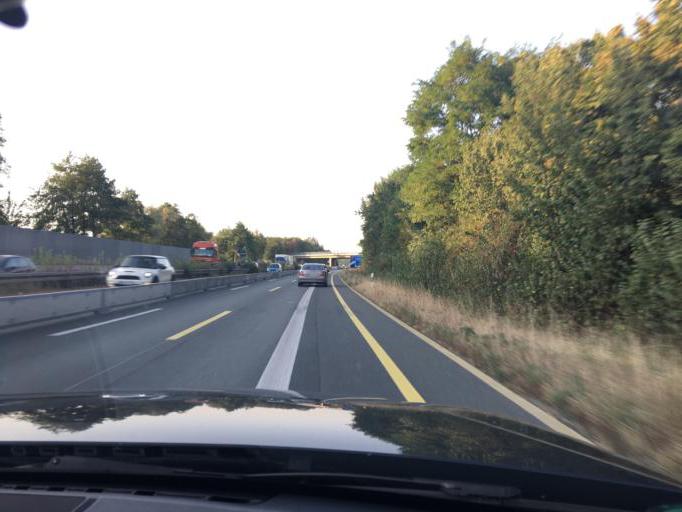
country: DE
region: Bavaria
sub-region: Upper Franconia
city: Forchheim
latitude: 49.7343
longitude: 11.0540
